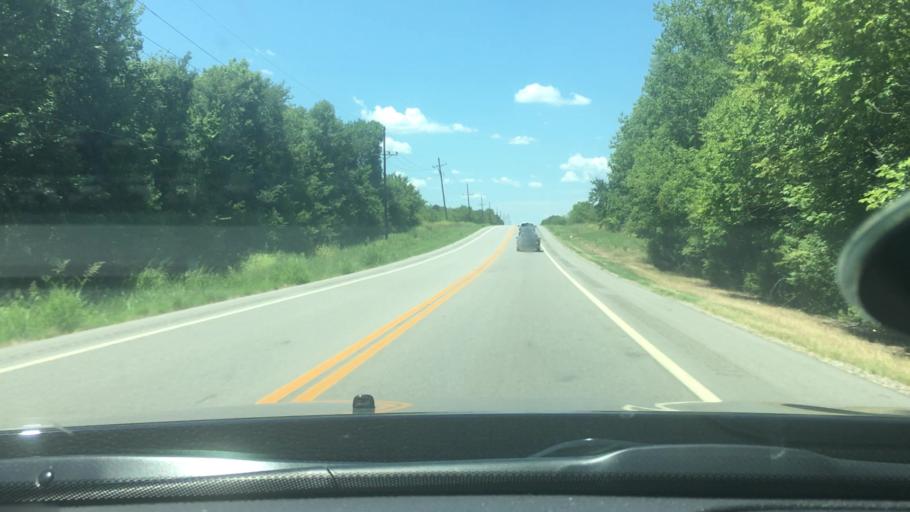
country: US
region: Oklahoma
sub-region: Bryan County
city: Durant
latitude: 34.0030
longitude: -96.2028
